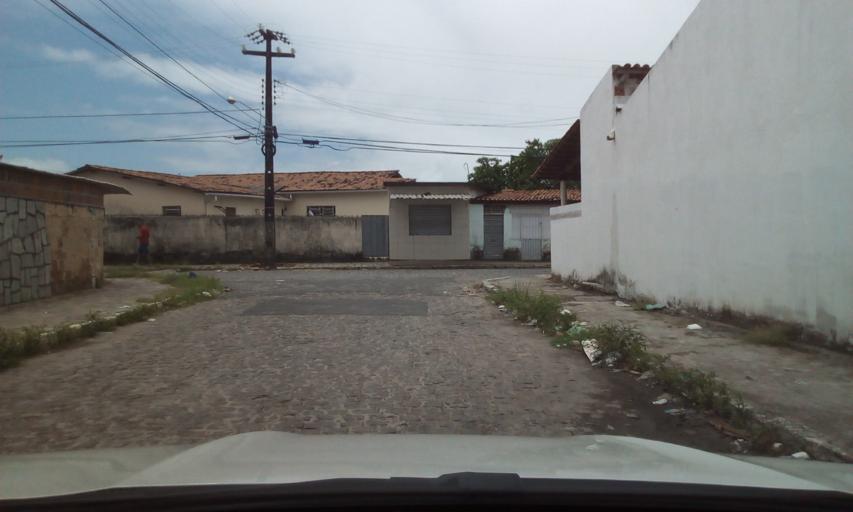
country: BR
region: Paraiba
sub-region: Joao Pessoa
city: Joao Pessoa
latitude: -7.1743
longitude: -34.8392
